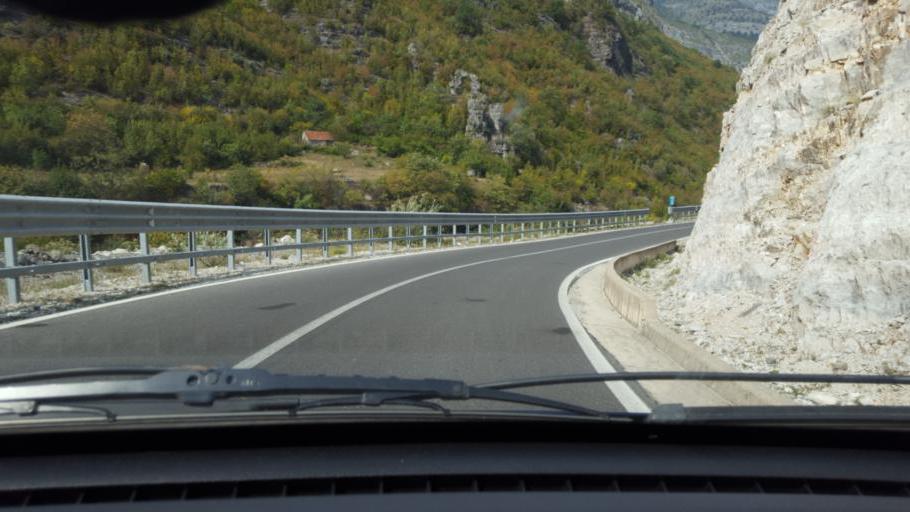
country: AL
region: Shkoder
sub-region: Rrethi i Malesia e Madhe
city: Kastrat
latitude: 42.4312
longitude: 19.5338
